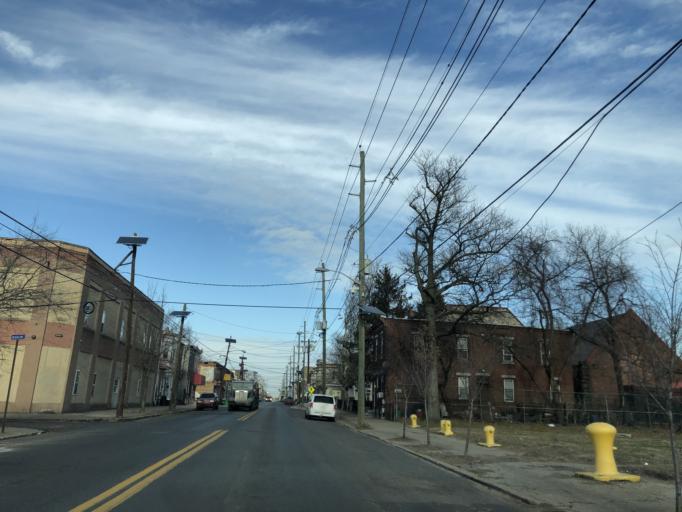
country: US
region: New Jersey
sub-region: Camden County
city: Camden
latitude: 39.9200
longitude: -75.1198
